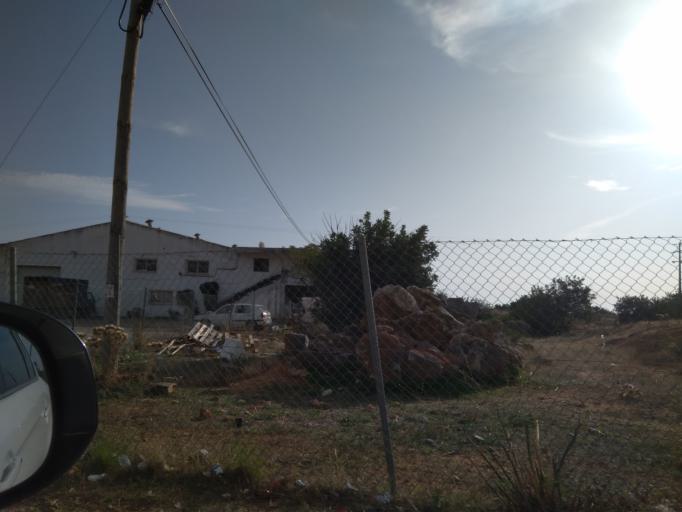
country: PT
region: Faro
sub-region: Faro
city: Santa Barbara de Nexe
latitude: 37.0913
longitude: -7.9378
